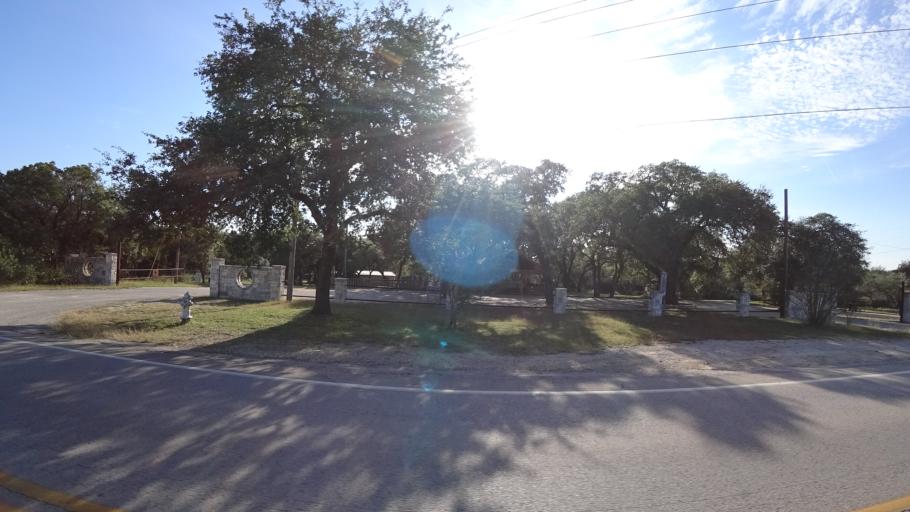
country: US
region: Texas
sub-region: Travis County
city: Bee Cave
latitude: 30.2444
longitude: -97.9247
